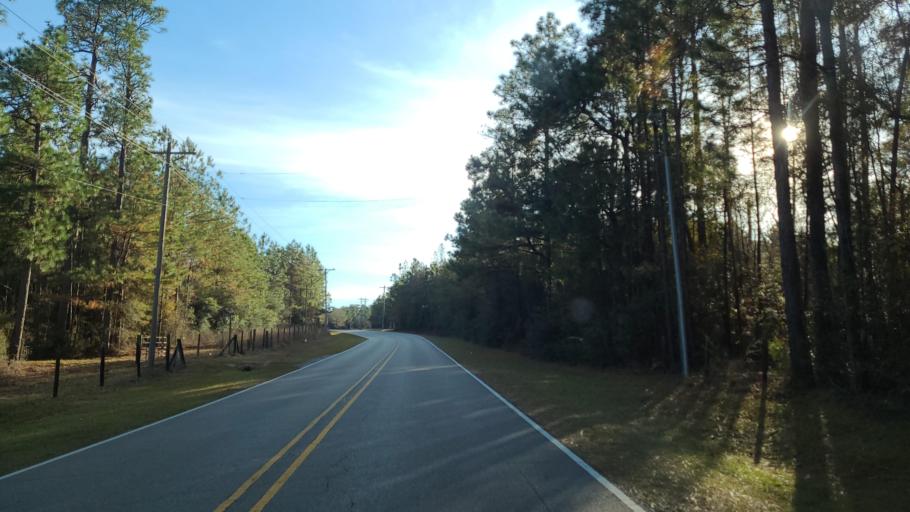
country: US
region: Mississippi
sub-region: Lamar County
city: Purvis
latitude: 31.1753
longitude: -89.2948
